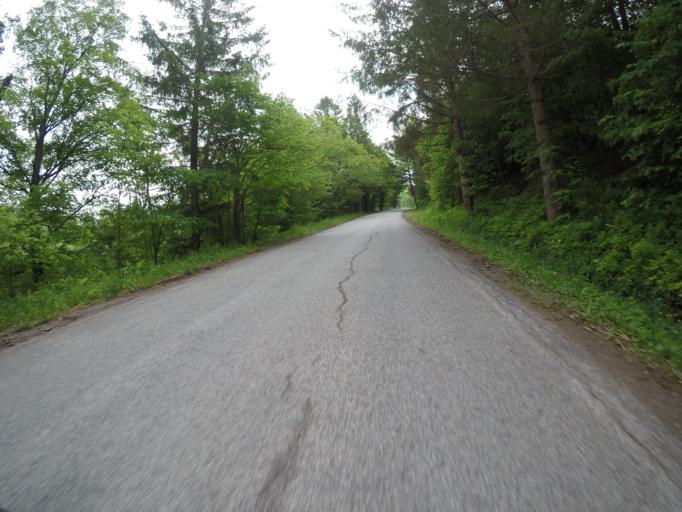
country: US
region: New York
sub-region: Delaware County
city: Stamford
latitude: 42.2631
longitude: -74.7240
